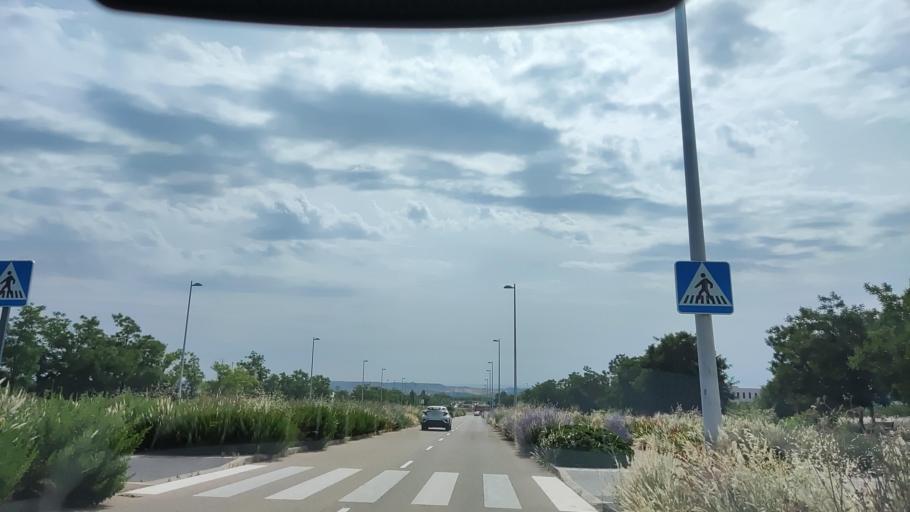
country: ES
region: Madrid
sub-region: Provincia de Madrid
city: Hortaleza
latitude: 40.4849
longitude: -3.6118
